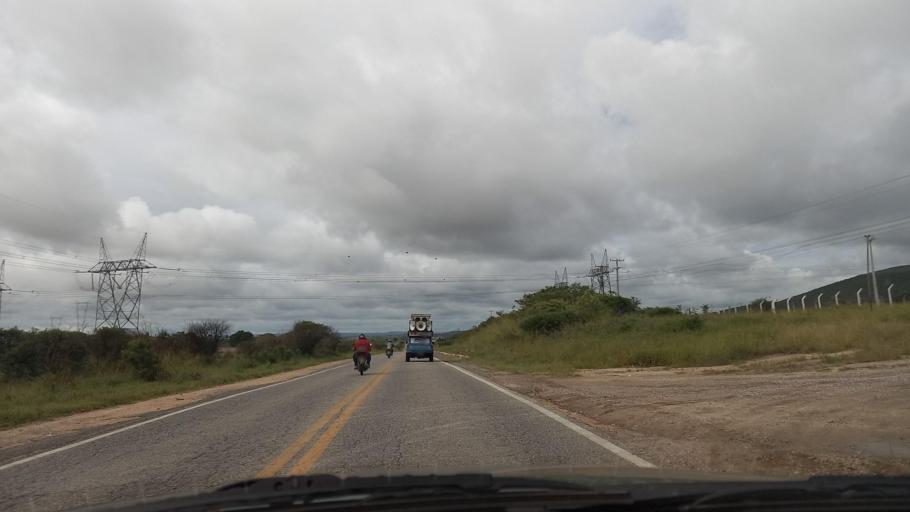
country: BR
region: Pernambuco
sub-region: Sao Joao
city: Sao Joao
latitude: -8.8798
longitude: -36.4021
